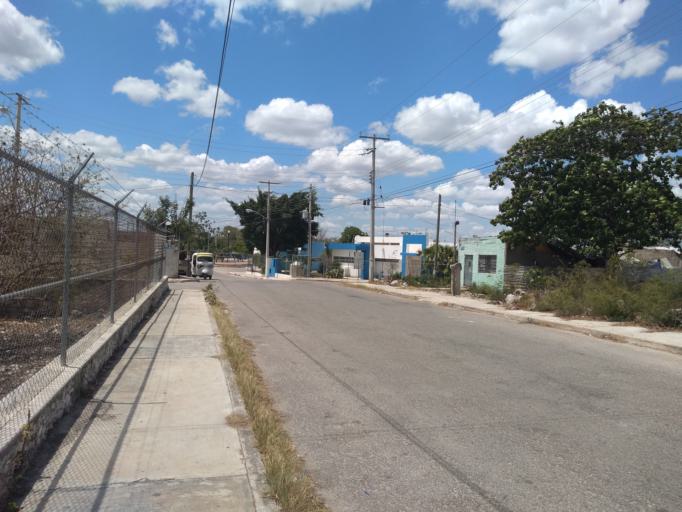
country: MX
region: Yucatan
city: Itzincab Palomeque
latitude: 20.9309
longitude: -89.6690
